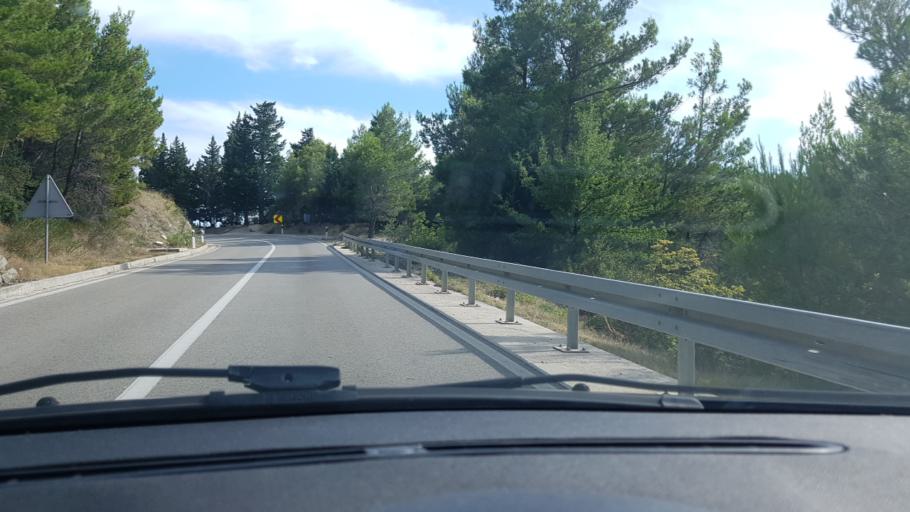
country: HR
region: Splitsko-Dalmatinska
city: Tucepi
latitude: 43.2820
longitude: 17.0431
